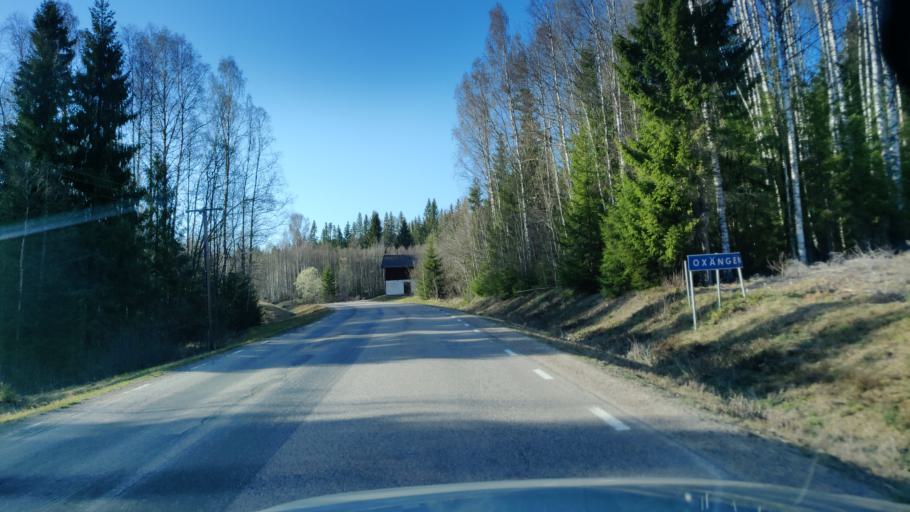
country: SE
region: Vaermland
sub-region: Munkfors Kommun
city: Munkfors
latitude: 59.9827
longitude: 13.4035
